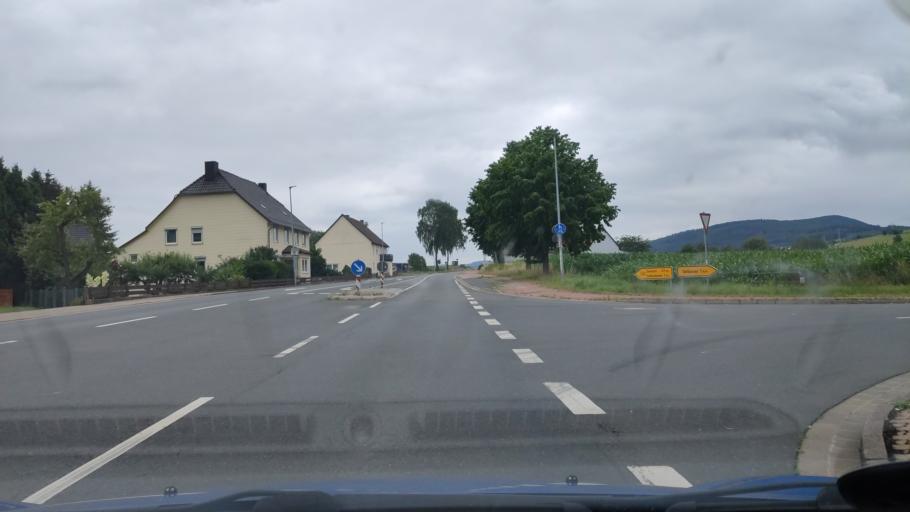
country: DE
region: Lower Saxony
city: Luerdissen
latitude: 51.9491
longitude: 9.6219
